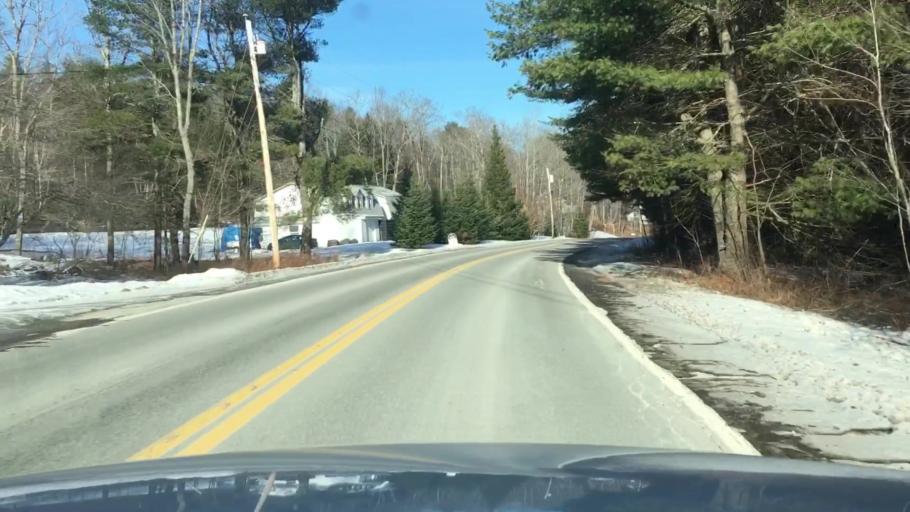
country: US
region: Maine
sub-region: Hancock County
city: Dedham
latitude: 44.6393
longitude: -68.6990
